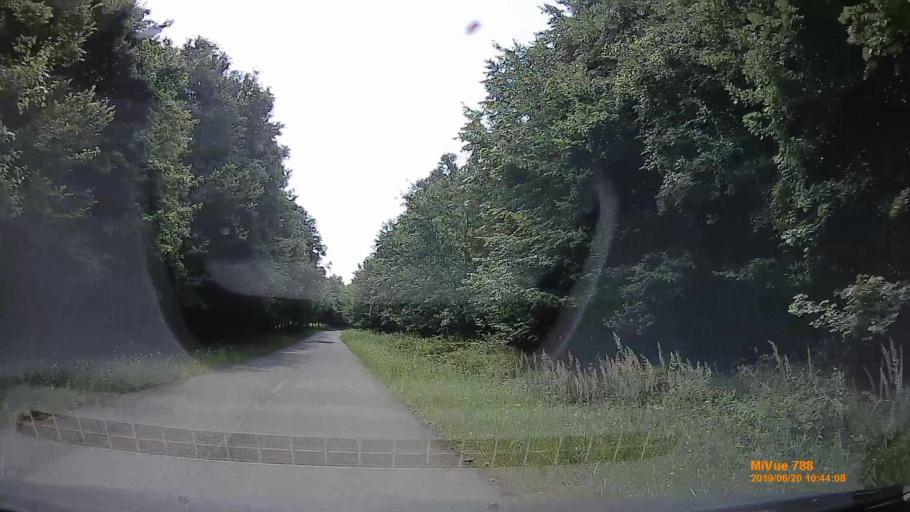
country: HU
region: Baranya
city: Hidas
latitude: 46.1900
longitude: 18.5640
